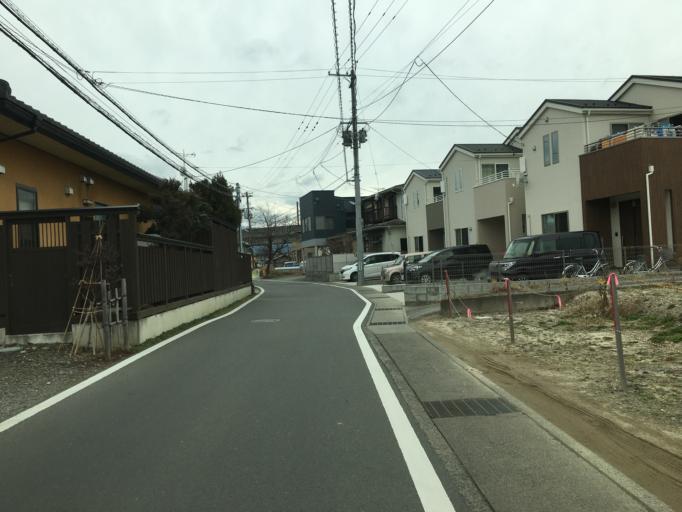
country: JP
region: Fukushima
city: Fukushima-shi
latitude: 37.7841
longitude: 140.4704
